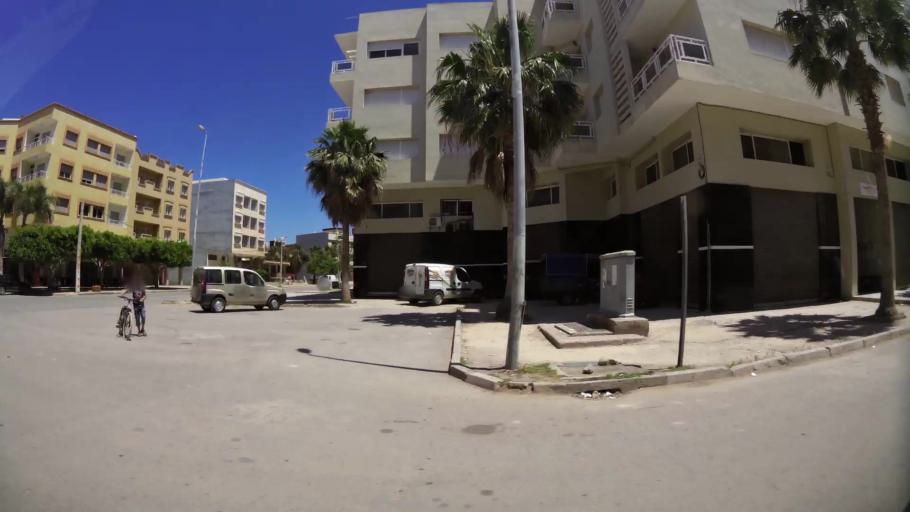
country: MA
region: Oriental
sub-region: Berkane-Taourirt
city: Madagh
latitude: 35.0759
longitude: -2.2240
